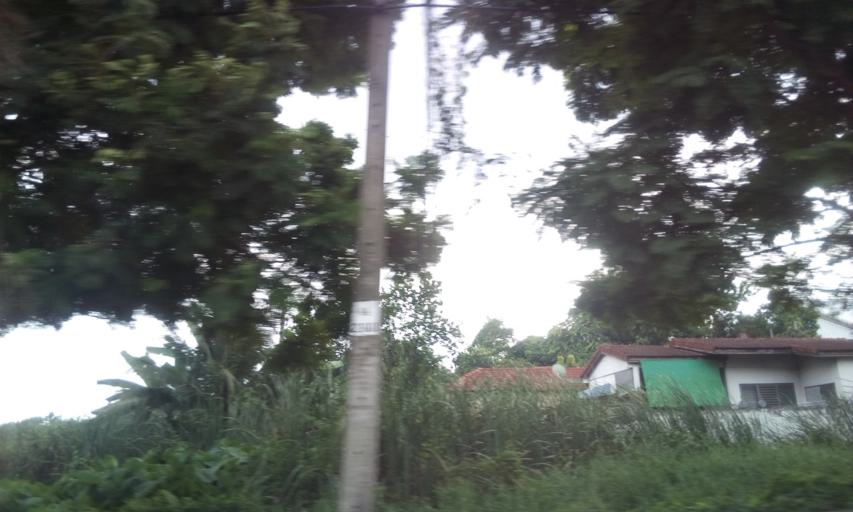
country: TH
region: Bangkok
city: Don Mueang
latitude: 13.9382
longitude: 100.5546
